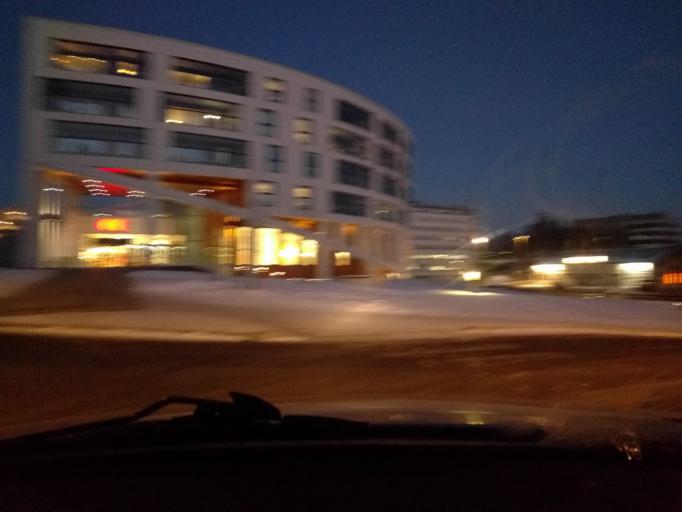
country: NO
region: Hedmark
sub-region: Hamar
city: Hamar
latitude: 60.7954
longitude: 11.0775
